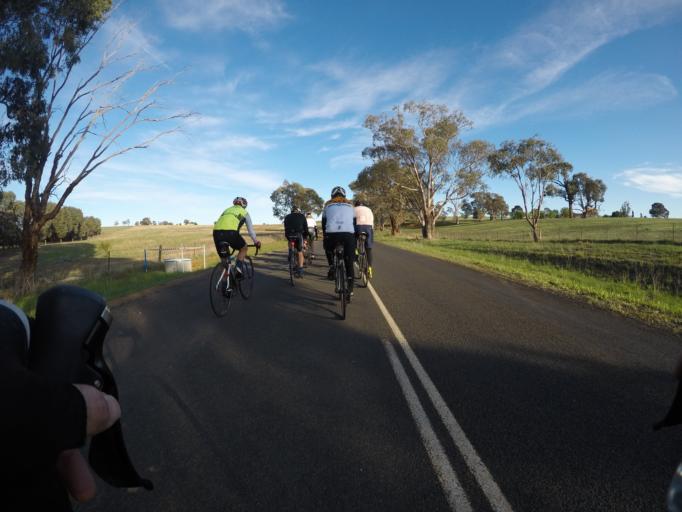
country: AU
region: New South Wales
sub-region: Cabonne
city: Molong
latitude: -33.0089
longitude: 148.7910
